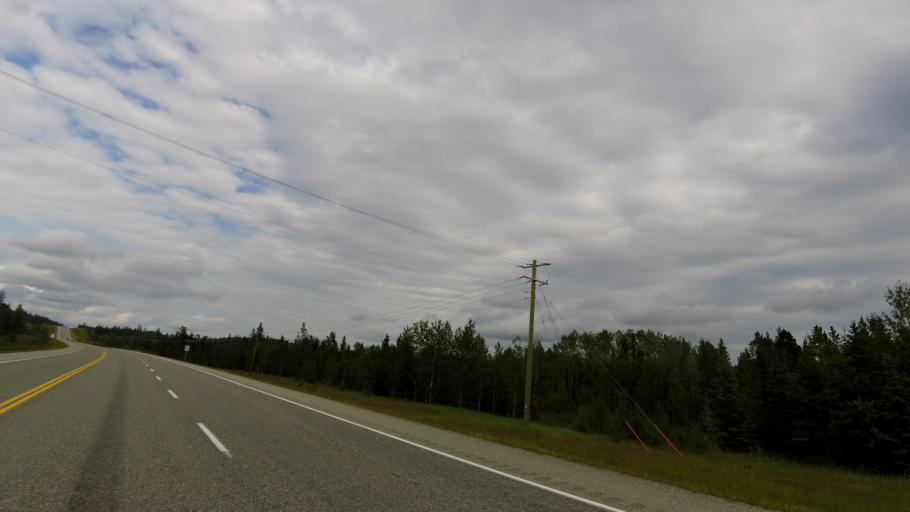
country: CA
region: Alberta
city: Rocky Mountain House
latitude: 52.4810
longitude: -115.6252
